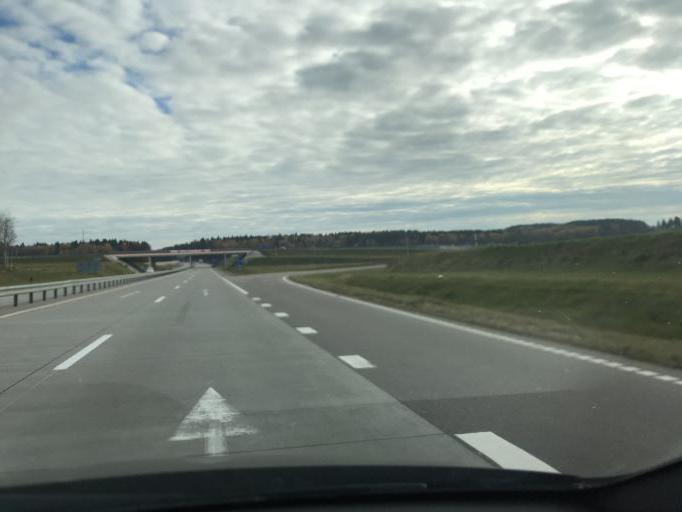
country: BY
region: Minsk
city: Zaslawye
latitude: 54.0687
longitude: 27.2874
